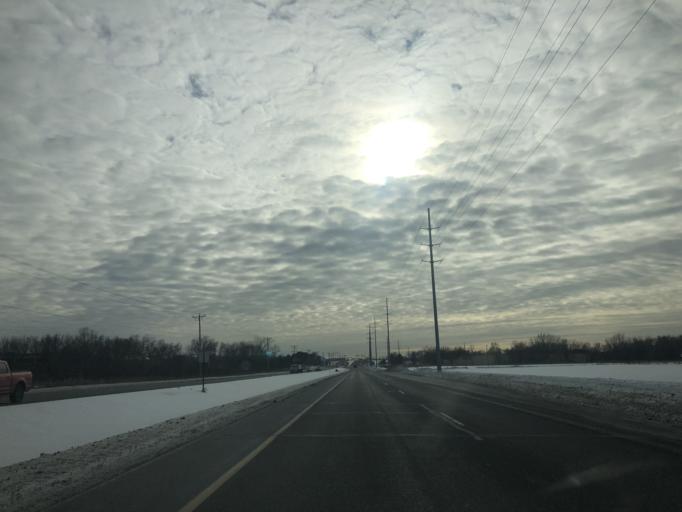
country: US
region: Minnesota
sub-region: Anoka County
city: Circle Pines
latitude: 45.1670
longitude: -93.1632
